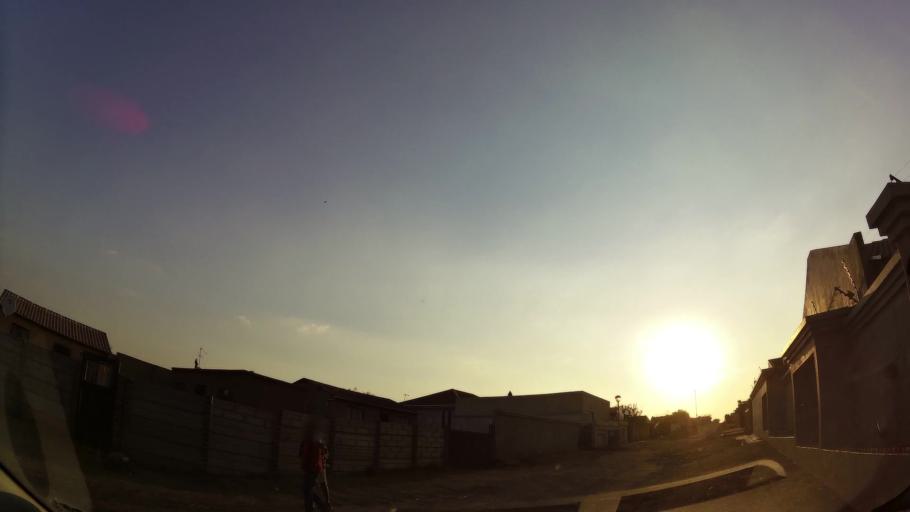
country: ZA
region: Gauteng
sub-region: Ekurhuleni Metropolitan Municipality
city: Benoni
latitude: -26.1639
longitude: 28.3818
